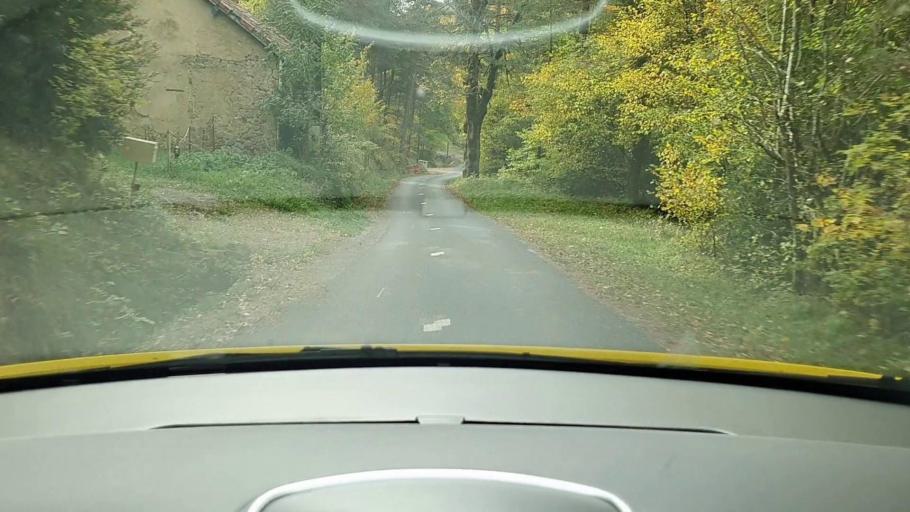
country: FR
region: Languedoc-Roussillon
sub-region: Departement de la Lozere
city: Meyrueis
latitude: 44.1188
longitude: 3.4329
